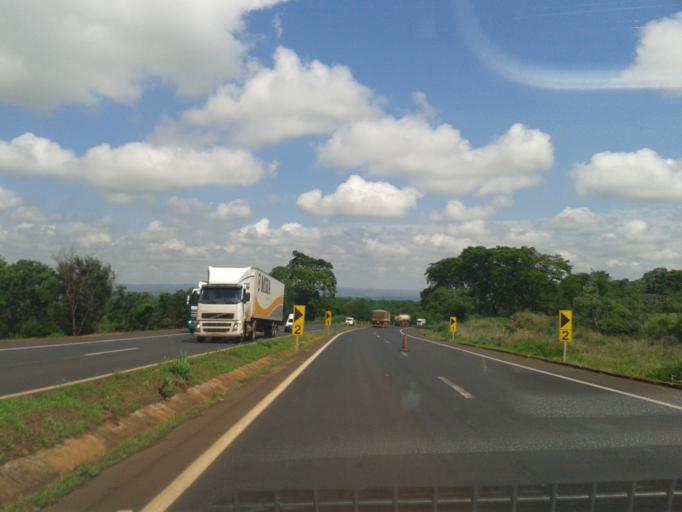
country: BR
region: Minas Gerais
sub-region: Centralina
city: Centralina
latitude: -18.6318
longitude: -49.1834
